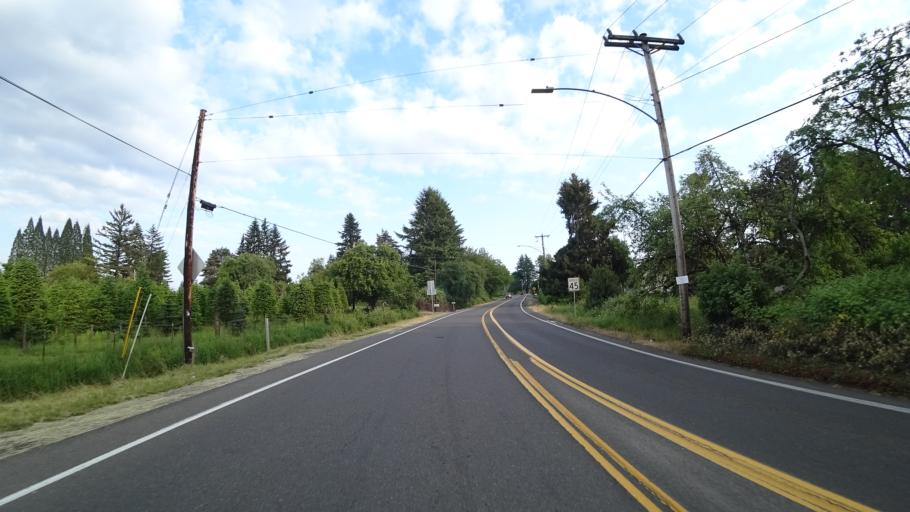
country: US
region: Oregon
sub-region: Clackamas County
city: Happy Valley
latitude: 45.4735
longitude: -122.4936
